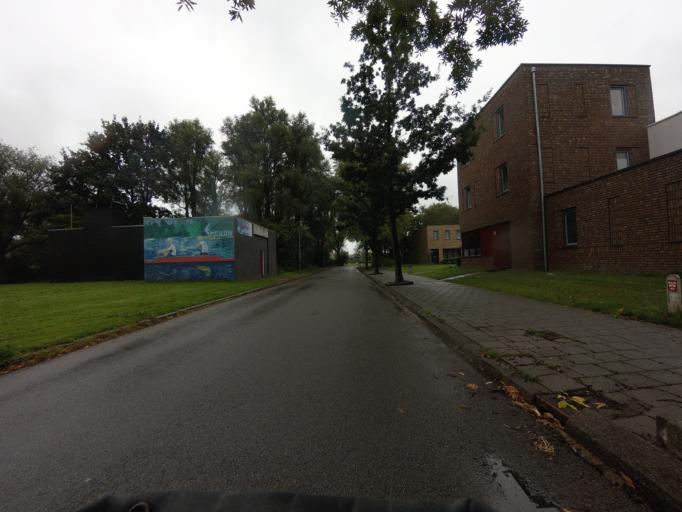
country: NL
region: Friesland
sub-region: Gemeente Leeuwarden
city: Bilgaard
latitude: 53.2165
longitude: 5.8056
